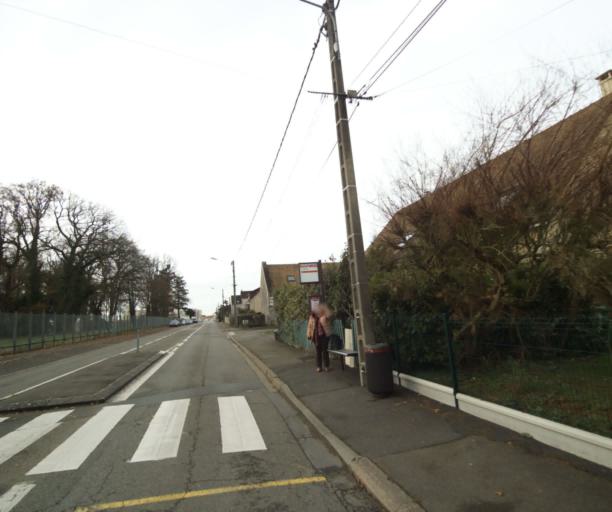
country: FR
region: Pays de la Loire
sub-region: Departement de la Sarthe
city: Le Mans
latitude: 48.0074
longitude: 0.2242
